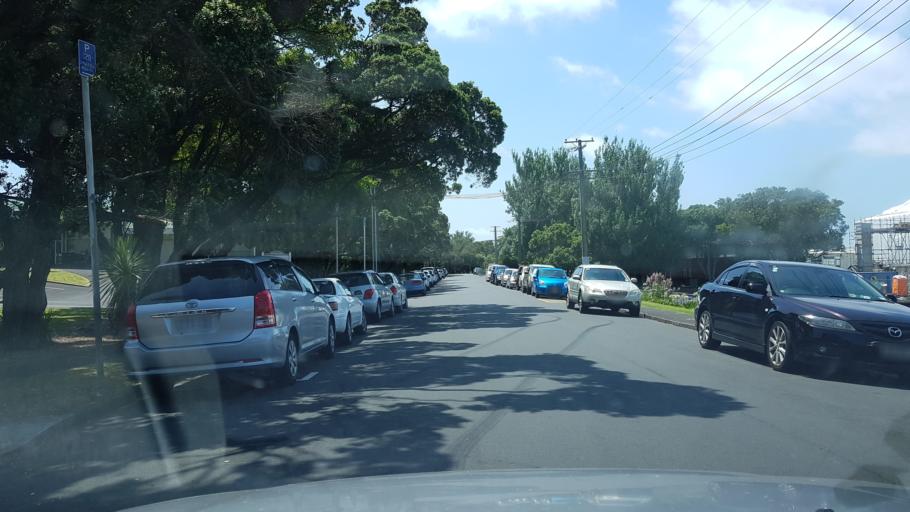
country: NZ
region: Auckland
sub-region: Auckland
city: North Shore
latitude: -36.8002
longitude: 174.7873
